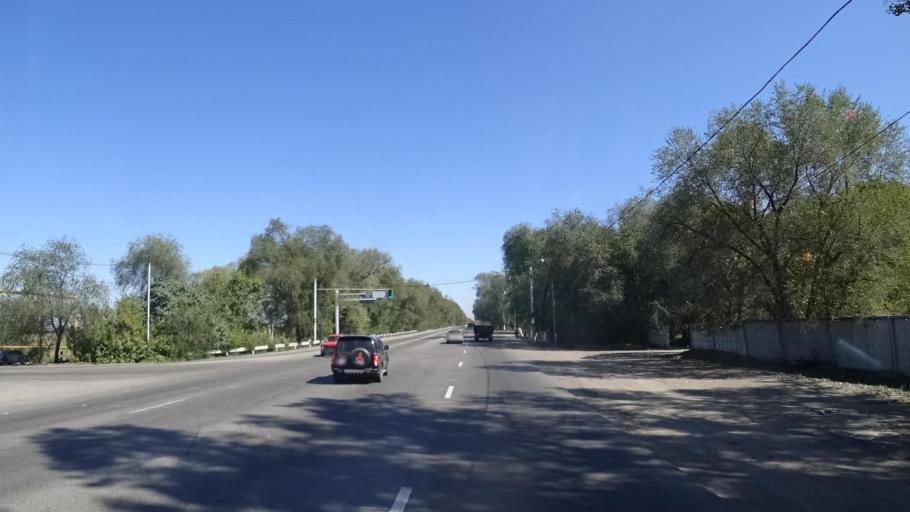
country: KZ
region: Almaty Oblysy
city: Energeticheskiy
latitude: 43.3665
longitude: 77.0868
